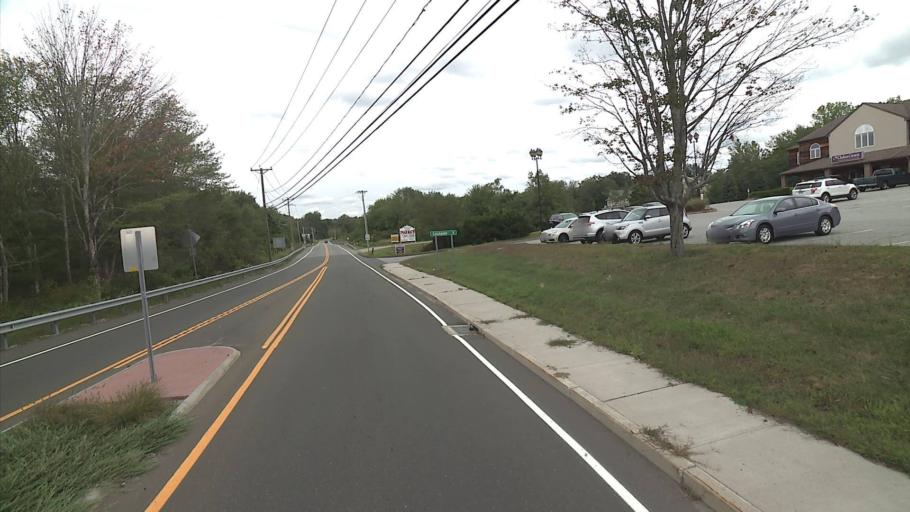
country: US
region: Connecticut
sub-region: New London County
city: Montville Center
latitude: 41.4771
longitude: -72.2652
